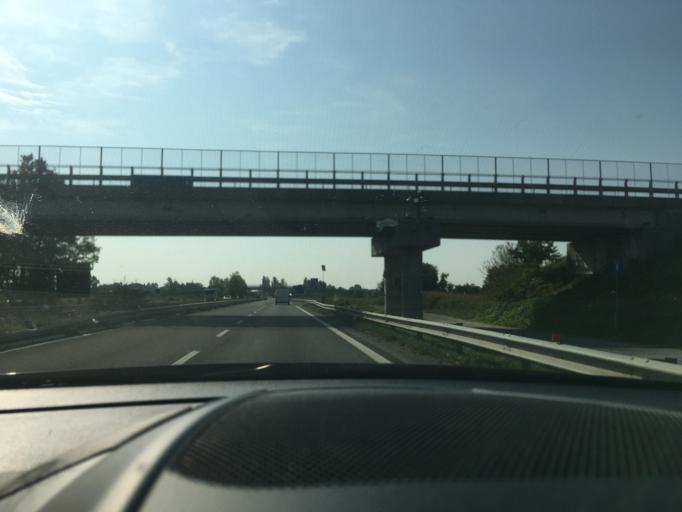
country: IT
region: Emilia-Romagna
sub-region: Forli-Cesena
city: San Mauro a Mare
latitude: 44.1537
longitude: 12.4409
